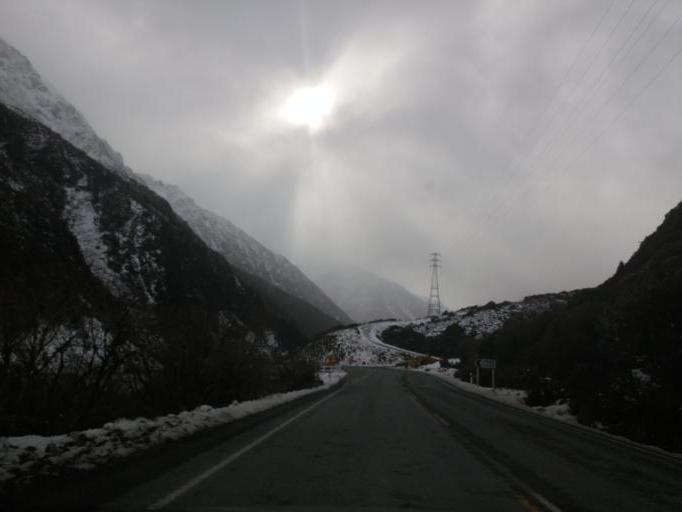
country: NZ
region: West Coast
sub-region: Grey District
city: Greymouth
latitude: -42.8916
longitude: 171.5573
